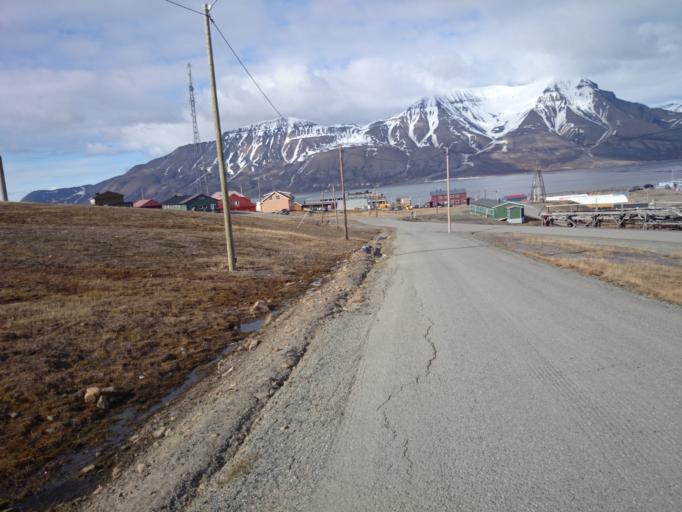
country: SJ
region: Svalbard
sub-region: Spitsbergen
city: Longyearbyen
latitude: 78.2202
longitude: 15.6202
